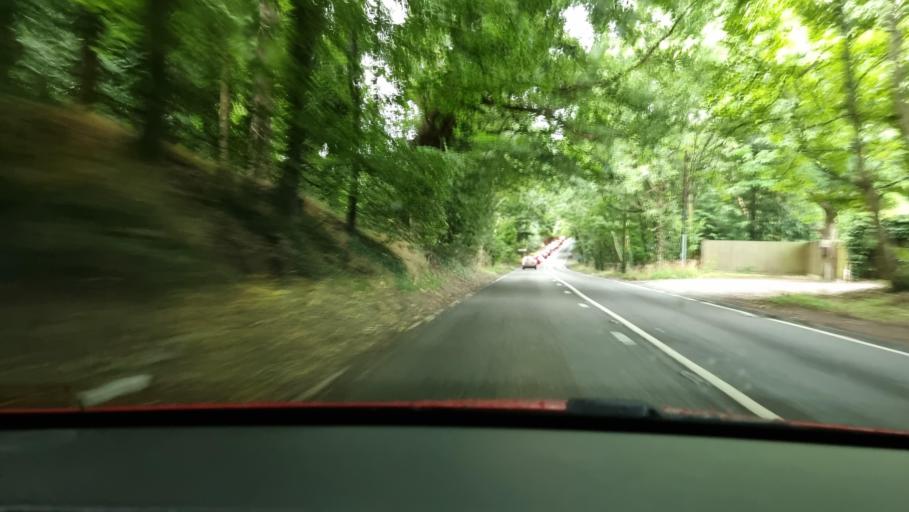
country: GB
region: England
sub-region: Hertfordshire
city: Berkhamsted
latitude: 51.7442
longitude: -0.5837
